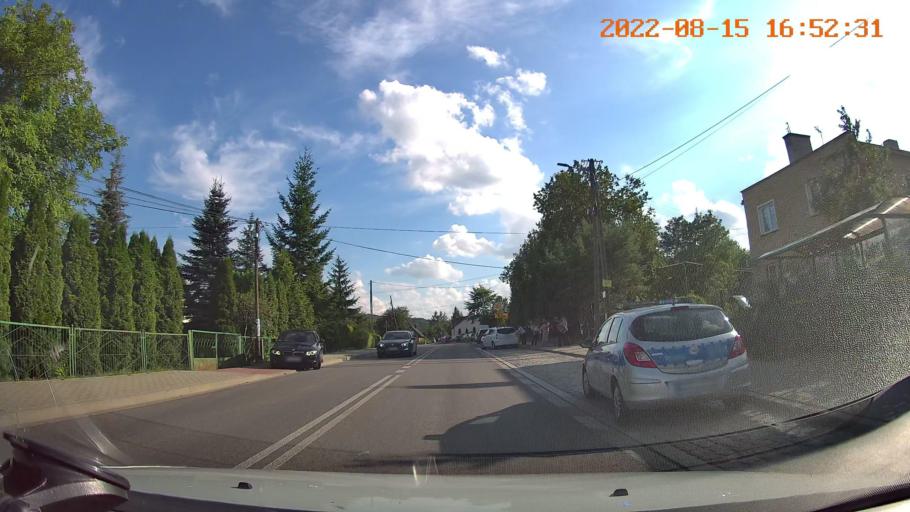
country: PL
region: Swietokrzyskie
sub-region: Powiat kielecki
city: Piekoszow
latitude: 50.8615
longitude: 20.4827
